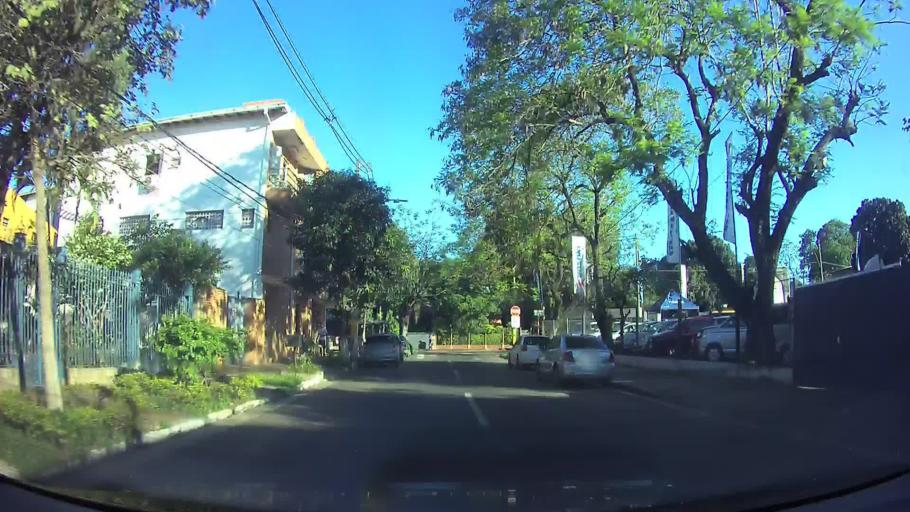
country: PY
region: Central
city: Fernando de la Mora
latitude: -25.3224
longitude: -57.5637
